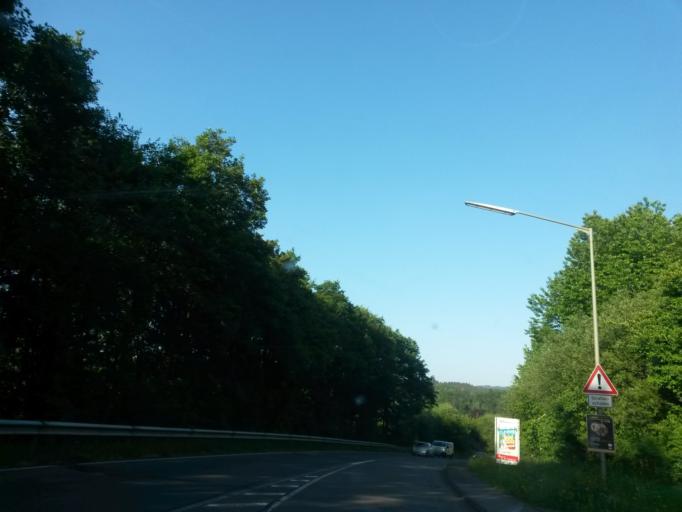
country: DE
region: North Rhine-Westphalia
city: Bergneustadt
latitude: 51.0128
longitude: 7.6450
